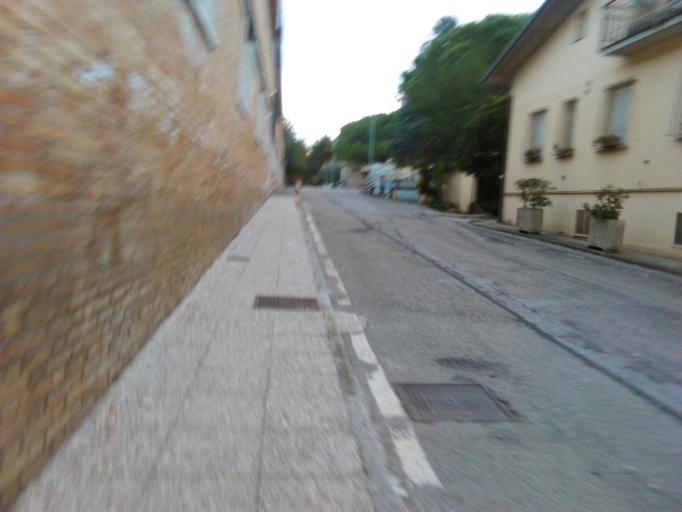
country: IT
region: Umbria
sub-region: Provincia di Perugia
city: Lacugnano
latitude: 43.0932
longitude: 12.3602
